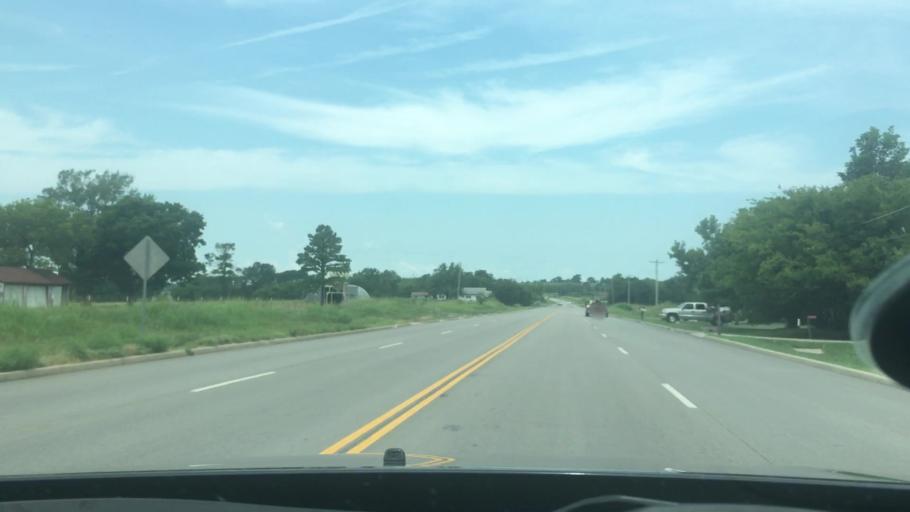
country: US
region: Oklahoma
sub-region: Seminole County
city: Seminole
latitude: 35.2651
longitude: -96.7161
